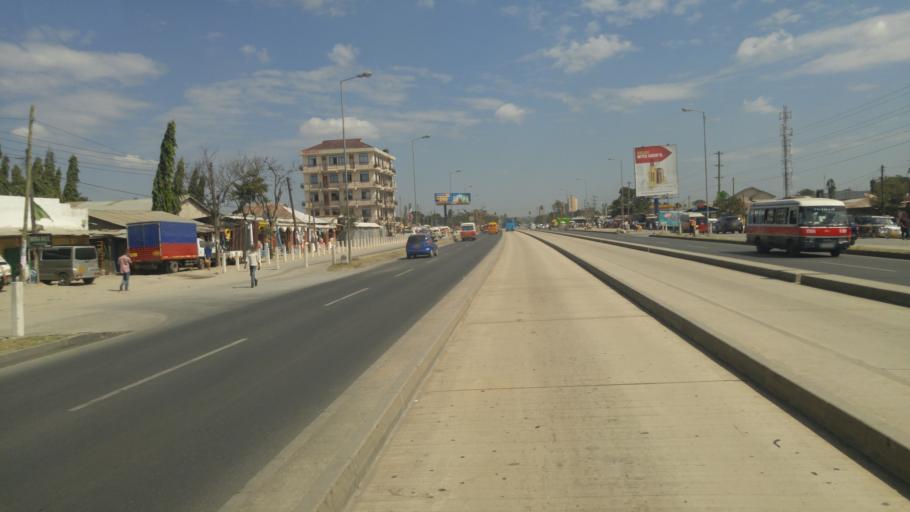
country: TZ
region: Dar es Salaam
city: Magomeni
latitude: -6.7978
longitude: 39.2285
